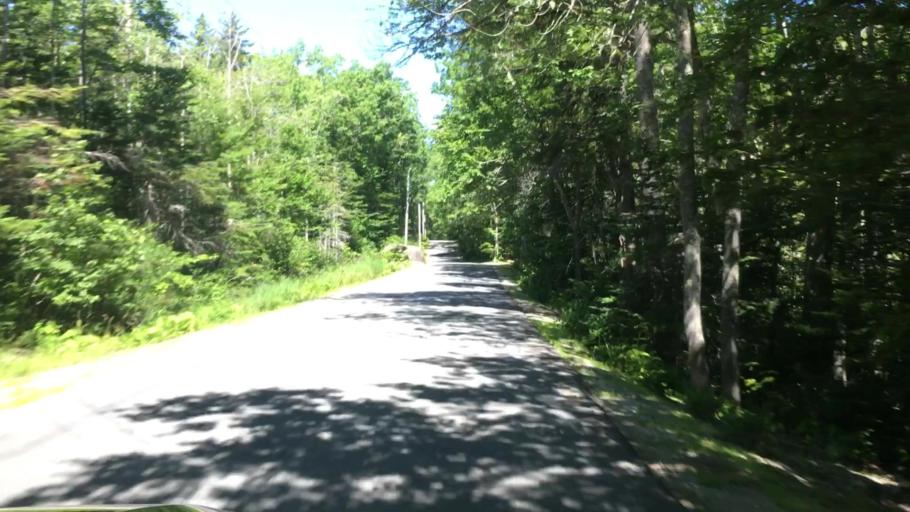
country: US
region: Maine
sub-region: Hancock County
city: Sedgwick
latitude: 44.3385
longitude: -68.6656
